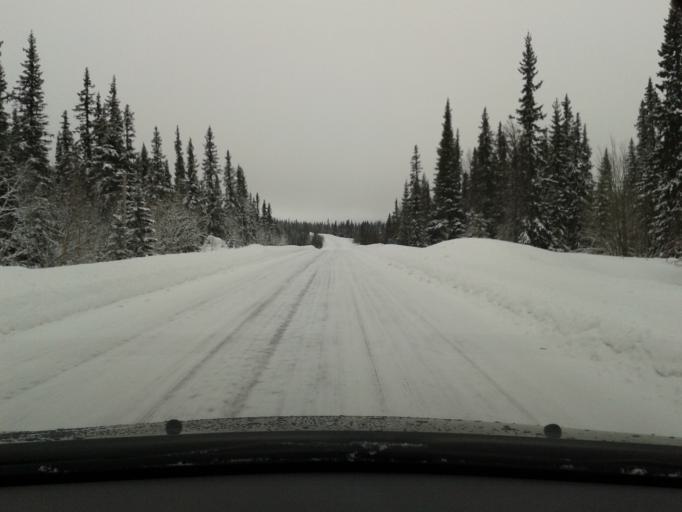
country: SE
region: Vaesterbotten
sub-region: Vilhelmina Kommun
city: Sjoberg
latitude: 65.1575
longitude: 15.8651
